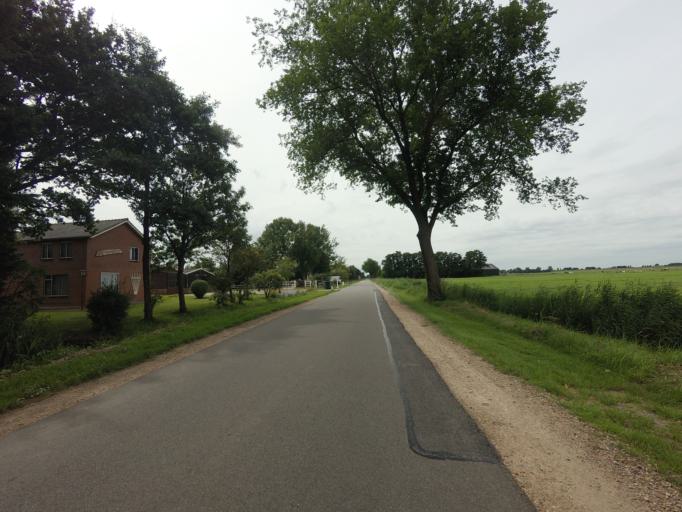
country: NL
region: Utrecht
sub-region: Gemeente De Ronde Venen
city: Mijdrecht
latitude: 52.2438
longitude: 4.8935
